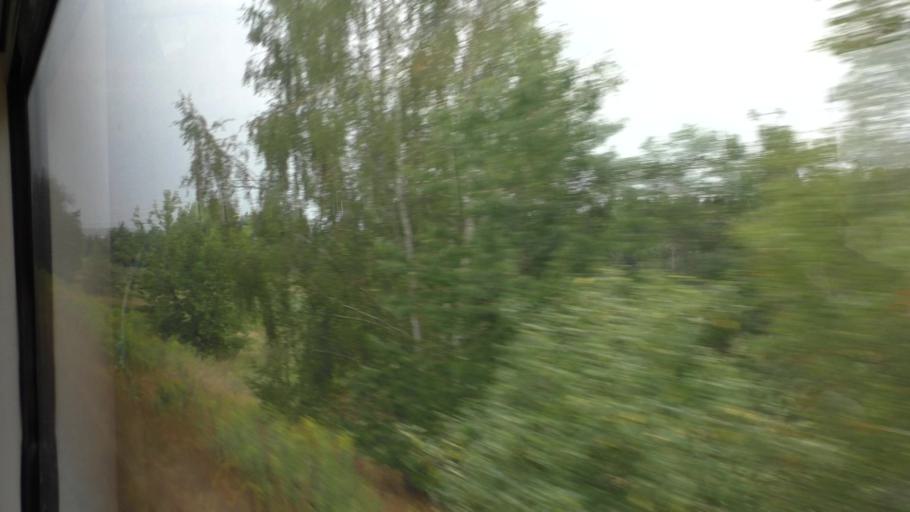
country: DE
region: Saxony
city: Goerlitz
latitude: 51.1095
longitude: 14.9764
